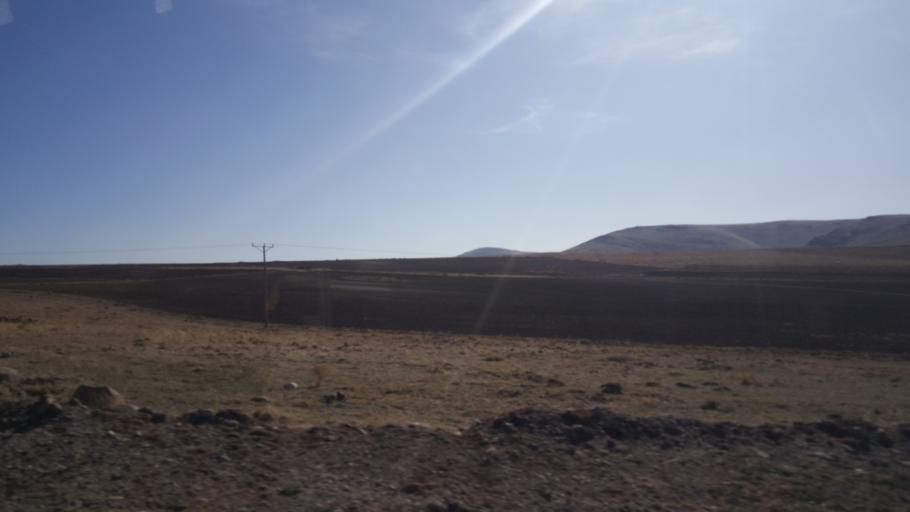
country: TR
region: Ankara
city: Yenice
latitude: 39.2426
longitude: 32.7163
